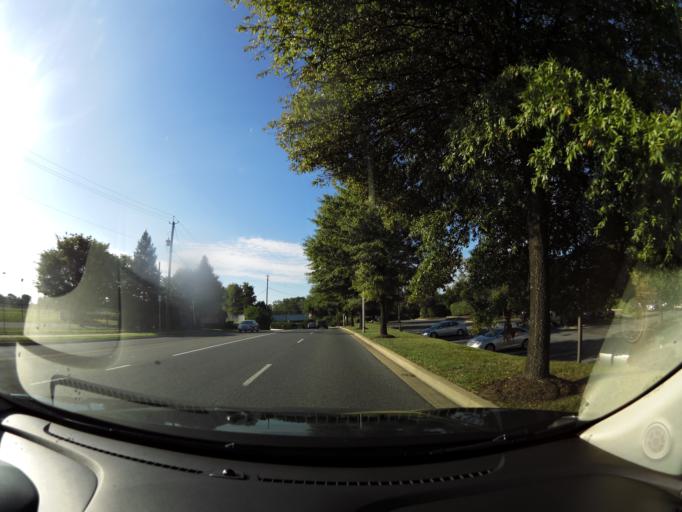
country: US
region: Maryland
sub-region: Montgomery County
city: Gaithersburg
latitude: 39.1474
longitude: -77.2141
